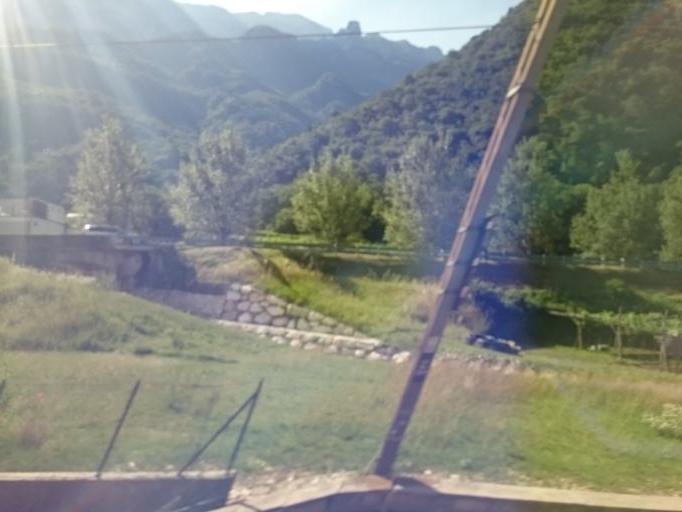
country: IT
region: Veneto
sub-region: Provincia di Verona
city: Rivalta
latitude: 45.6888
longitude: 10.9182
